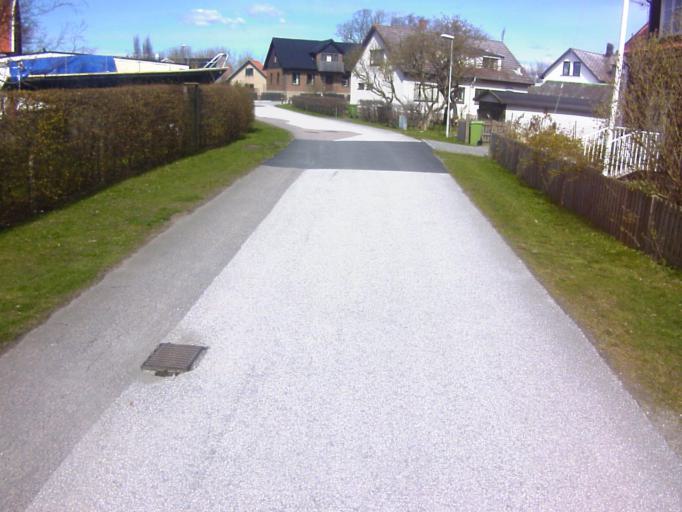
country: SE
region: Skane
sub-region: Kavlinge Kommun
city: Hofterup
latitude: 55.7562
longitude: 12.9084
